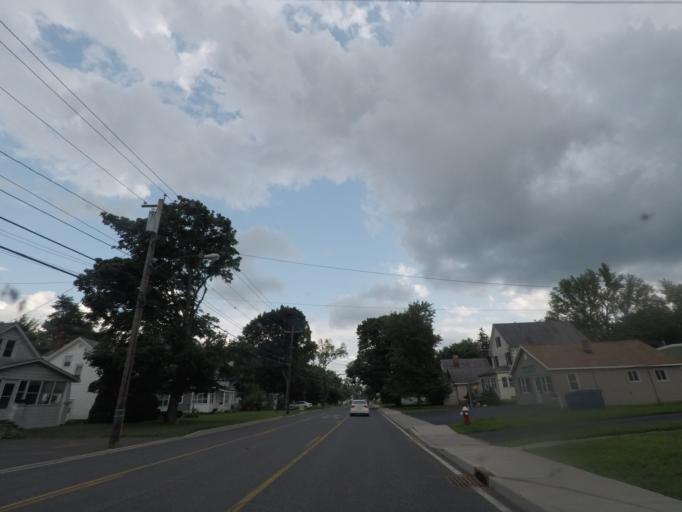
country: US
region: New York
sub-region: Albany County
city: West Albany
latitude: 42.6916
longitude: -73.7850
